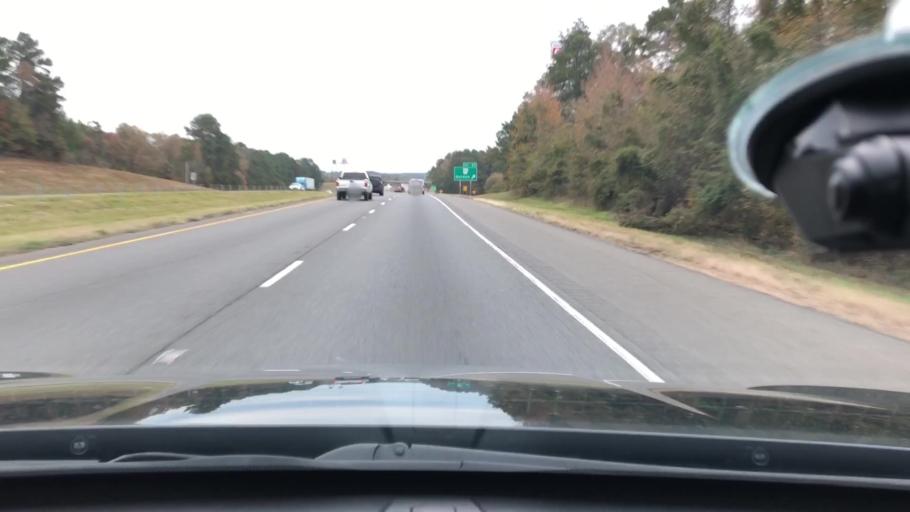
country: US
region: Arkansas
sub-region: Clark County
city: Gurdon
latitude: 33.9922
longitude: -93.1885
